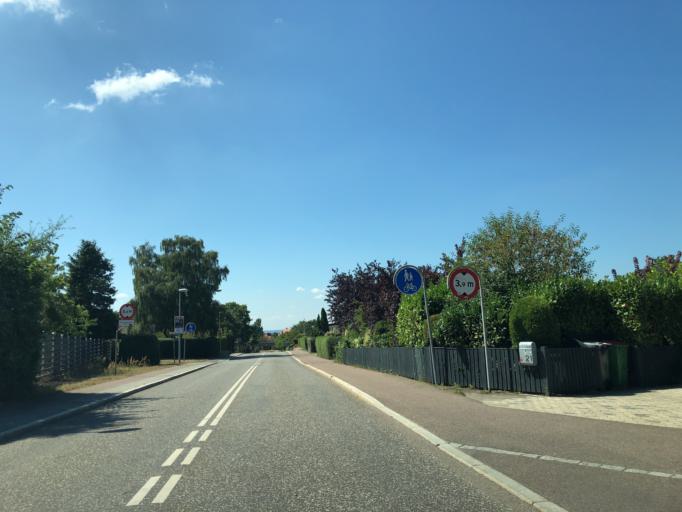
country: DK
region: Capital Region
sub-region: Halsnaes Kommune
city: Hundested
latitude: 55.9603
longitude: 11.8588
